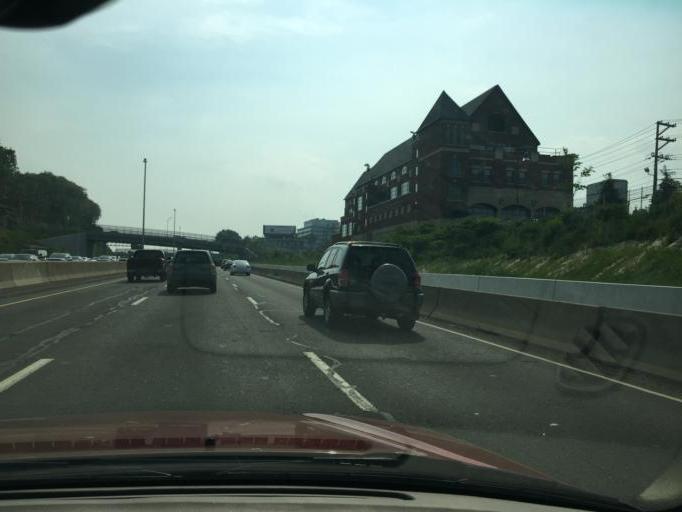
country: US
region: Connecticut
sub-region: Fairfield County
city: Norwalk
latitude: 41.1057
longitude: -73.4259
